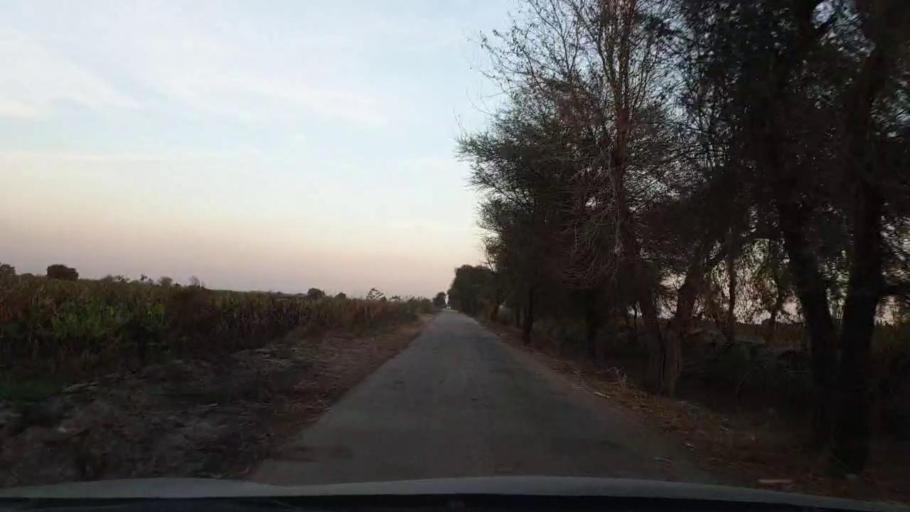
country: PK
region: Sindh
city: Tando Allahyar
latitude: 25.5949
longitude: 68.7049
